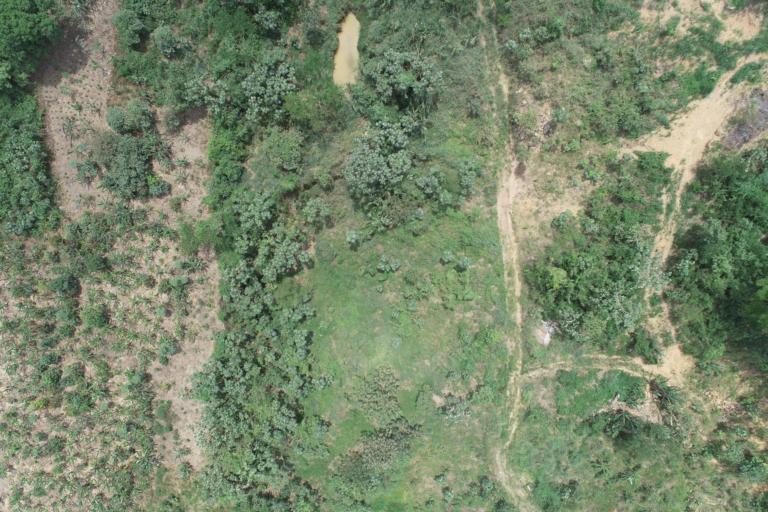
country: BO
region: La Paz
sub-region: Provincia Larecaja
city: Guanay
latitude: -15.7671
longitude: -67.6634
